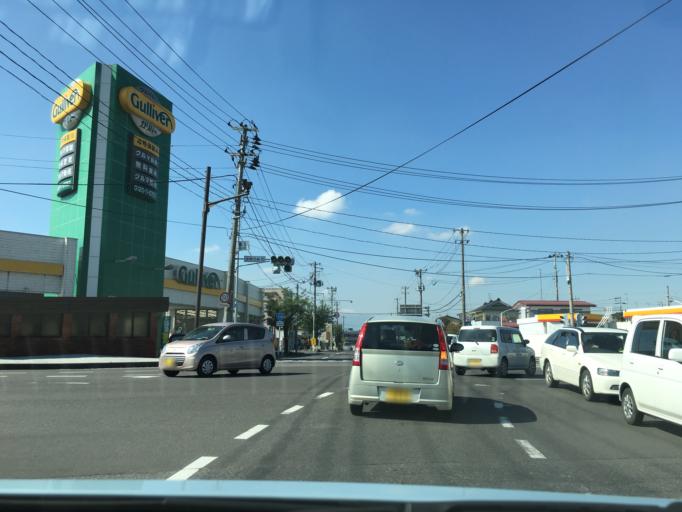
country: JP
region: Fukushima
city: Sukagawa
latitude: 37.2886
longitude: 140.3686
